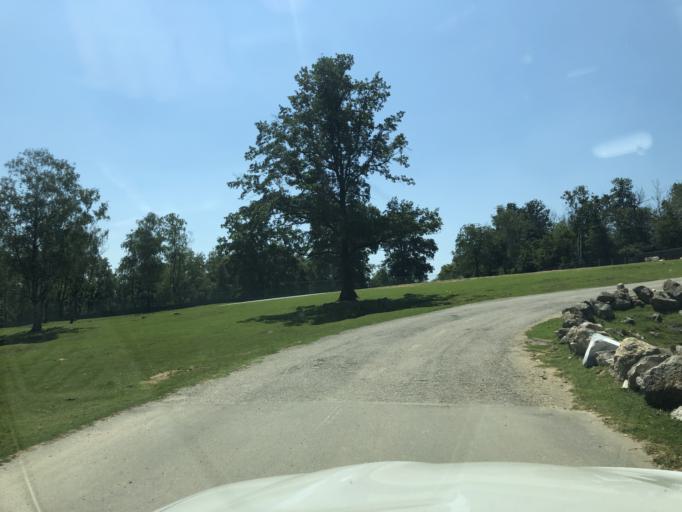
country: IT
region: Piedmont
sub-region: Provincia di Novara
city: Mezzomerico
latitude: 45.6400
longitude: 8.6106
